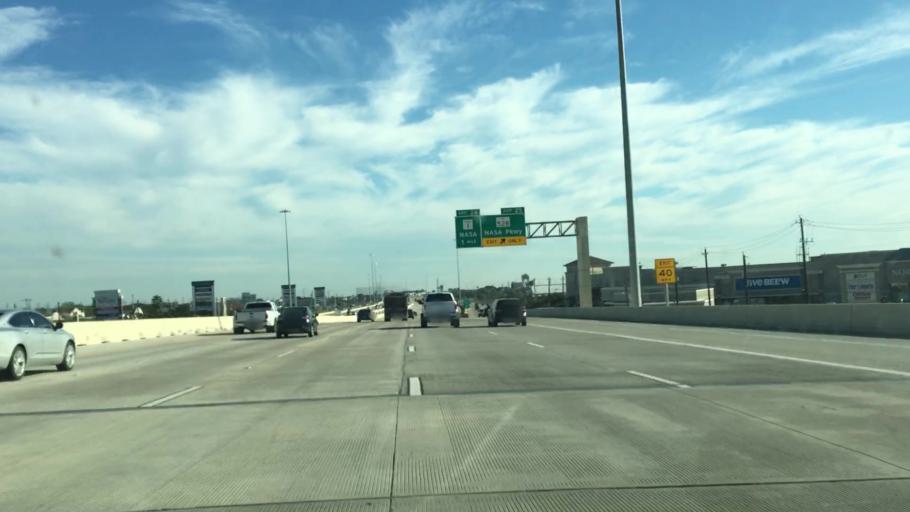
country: US
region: Texas
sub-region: Harris County
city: Webster
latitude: 29.5398
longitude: -95.1412
